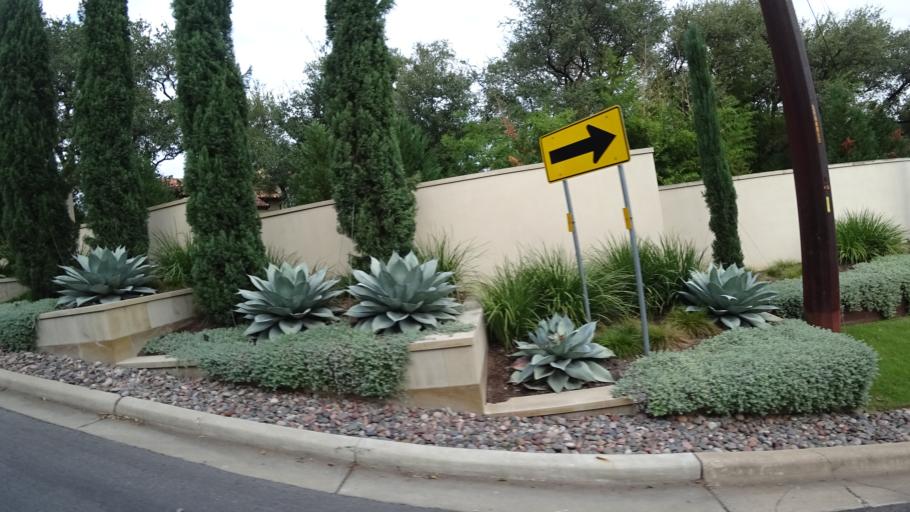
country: US
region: Texas
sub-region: Travis County
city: Rollingwood
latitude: 30.2797
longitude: -97.7820
